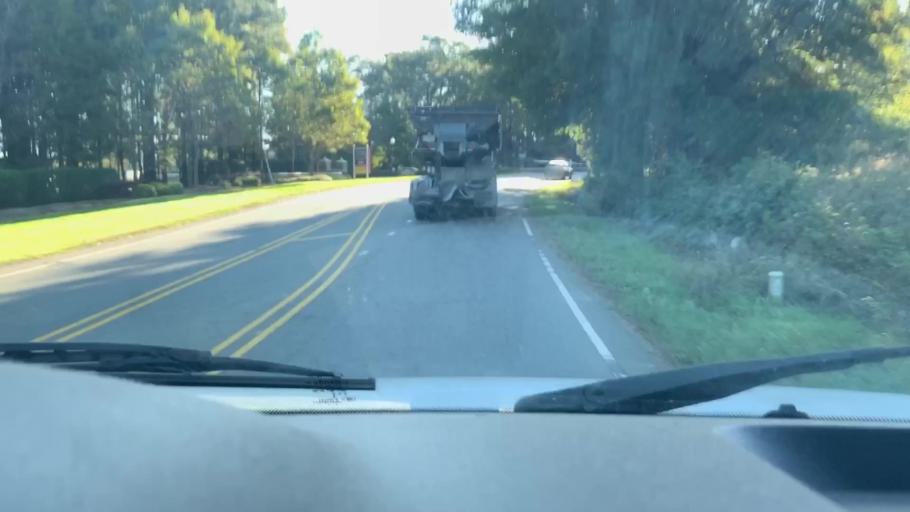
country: US
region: North Carolina
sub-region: Mecklenburg County
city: Huntersville
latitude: 35.4303
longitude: -80.7598
